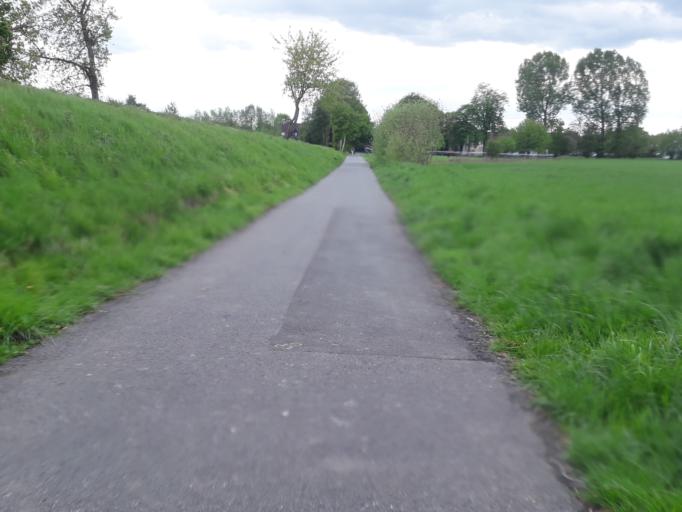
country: DE
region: North Rhine-Westphalia
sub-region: Regierungsbezirk Detmold
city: Paderborn
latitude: 51.7489
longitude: 8.7708
